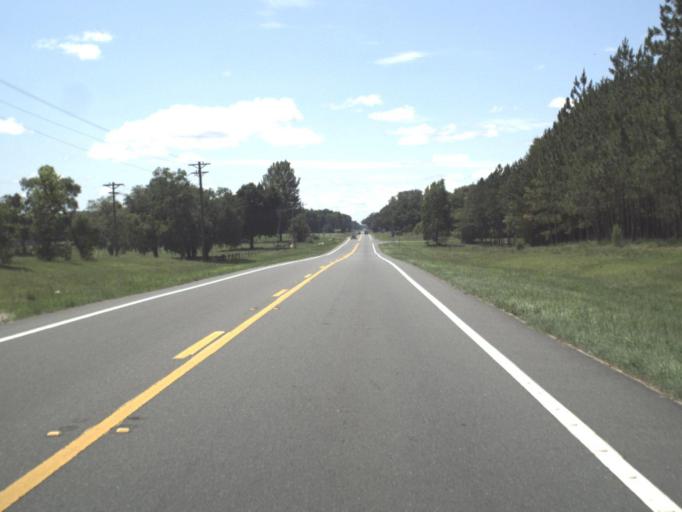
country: US
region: Florida
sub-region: Lafayette County
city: Mayo
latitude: 30.0953
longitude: -83.2343
